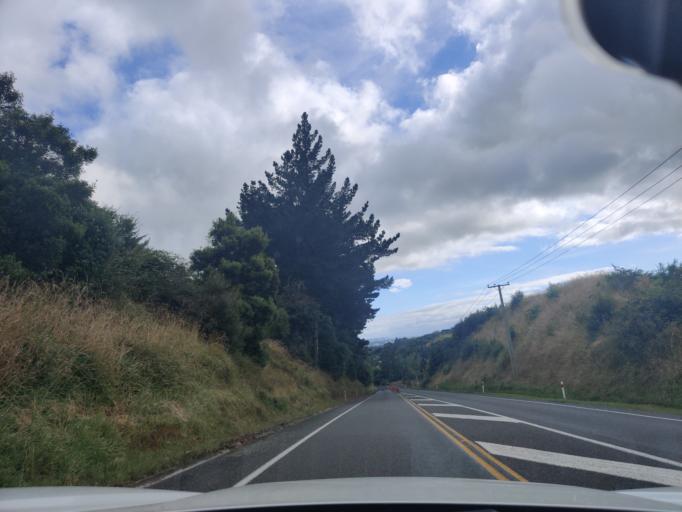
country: NZ
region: Manawatu-Wanganui
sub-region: Palmerston North City
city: Palmerston North
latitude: -40.3812
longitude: 175.6471
